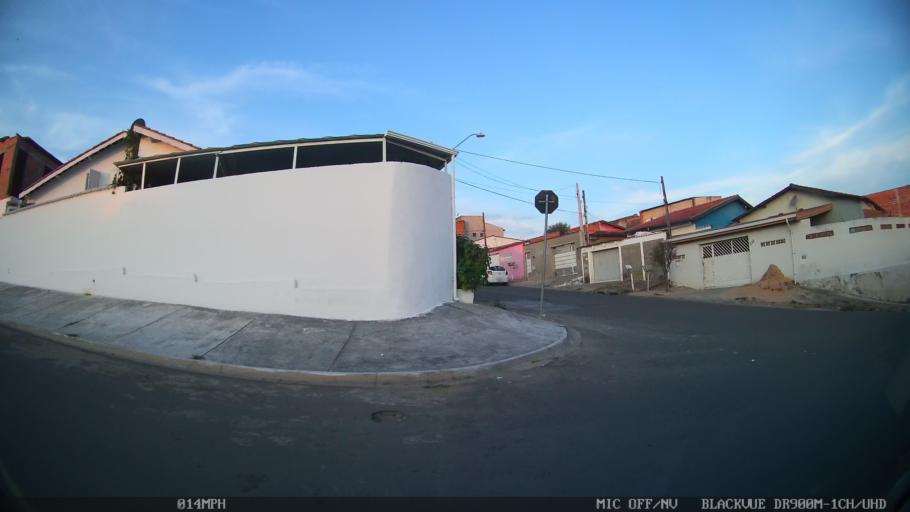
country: BR
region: Sao Paulo
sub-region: Campinas
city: Campinas
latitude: -22.9836
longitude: -47.1235
